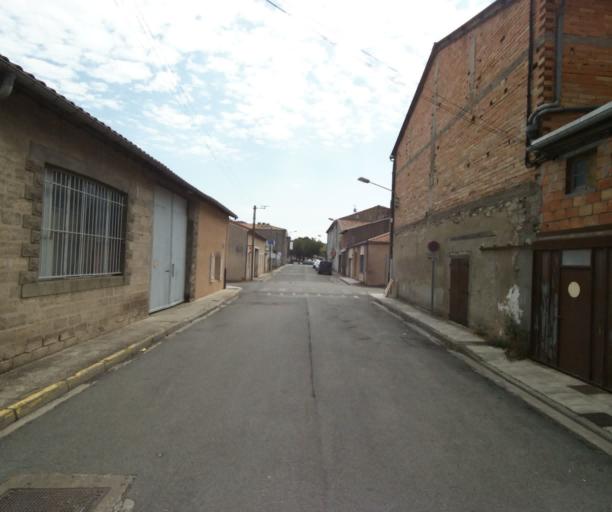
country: FR
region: Midi-Pyrenees
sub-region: Departement de la Haute-Garonne
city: Revel
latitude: 43.4608
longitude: 2.0033
